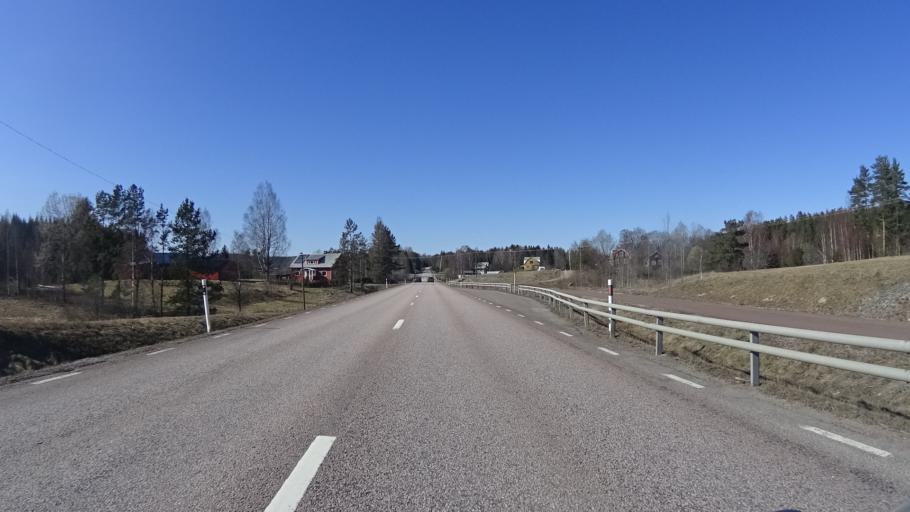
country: SE
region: Vaermland
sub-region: Karlstads Kommun
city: Edsvalla
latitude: 59.5573
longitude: 13.0382
